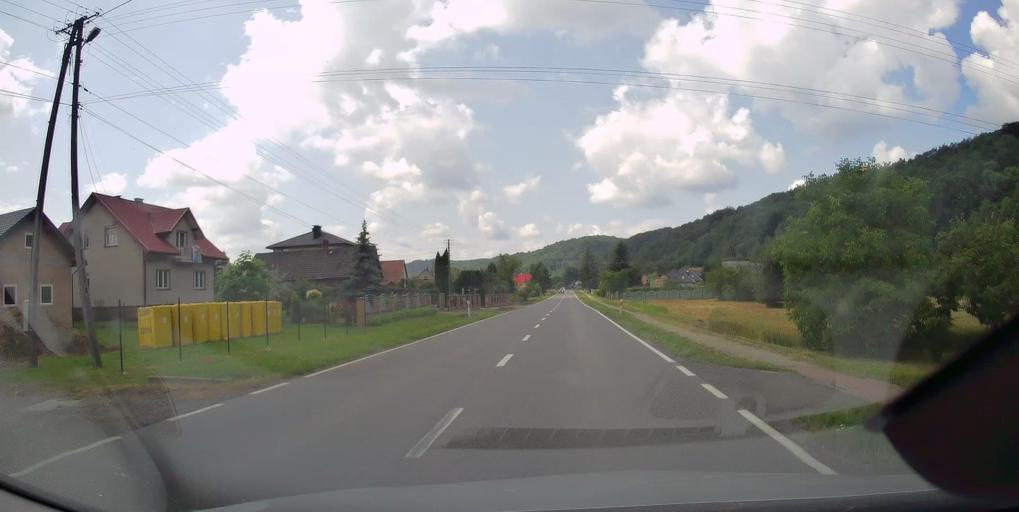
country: PL
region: Lesser Poland Voivodeship
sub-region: Powiat tarnowski
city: Wielka Wies
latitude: 49.9200
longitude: 20.8252
